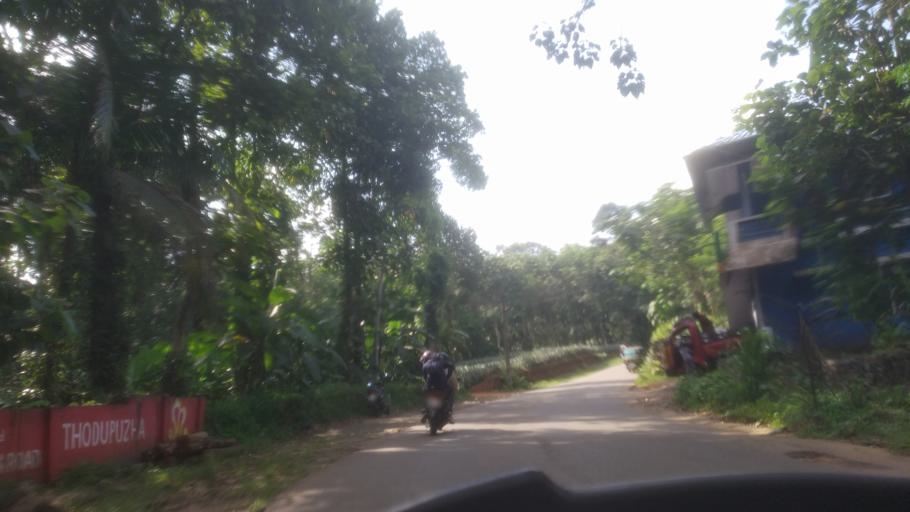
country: IN
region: Kerala
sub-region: Ernakulam
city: Muvattupula
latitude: 9.9987
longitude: 76.6359
